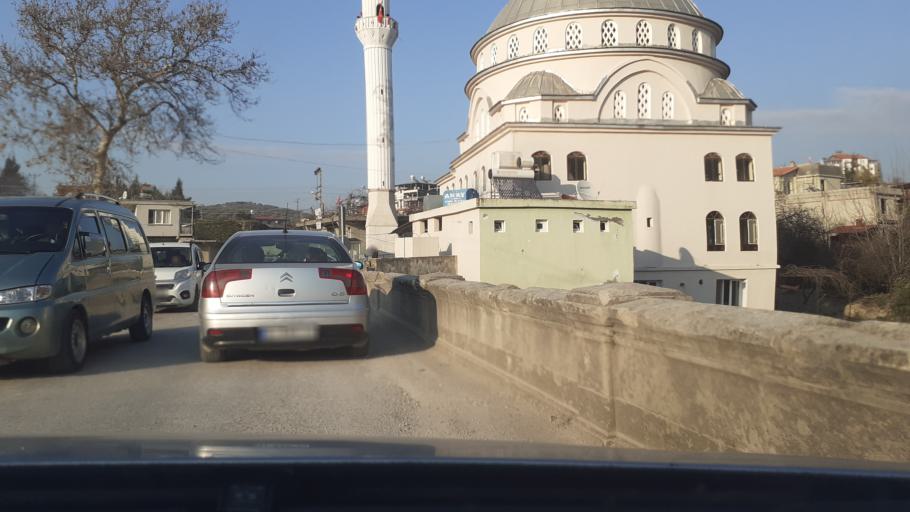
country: TR
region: Hatay
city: Fatikli
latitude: 36.1125
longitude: 36.2620
